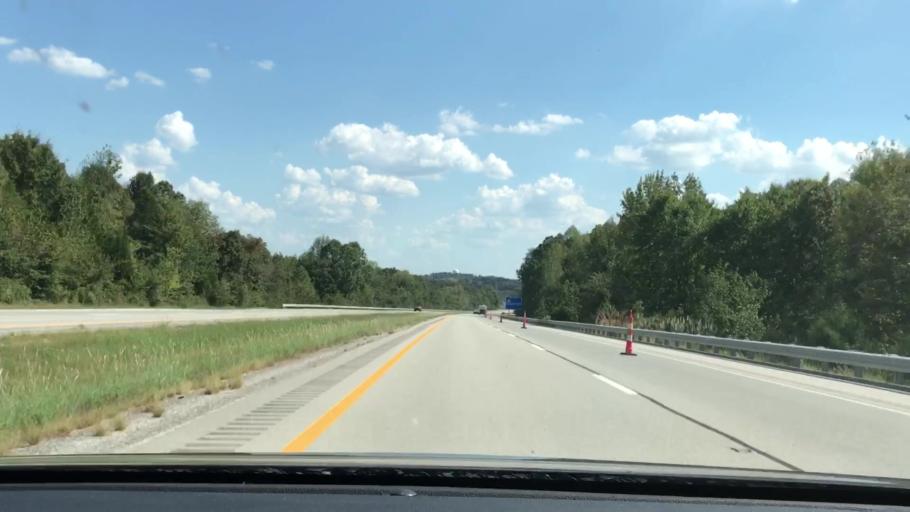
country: US
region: Kentucky
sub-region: Butler County
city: Morgantown
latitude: 37.2239
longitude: -86.7188
